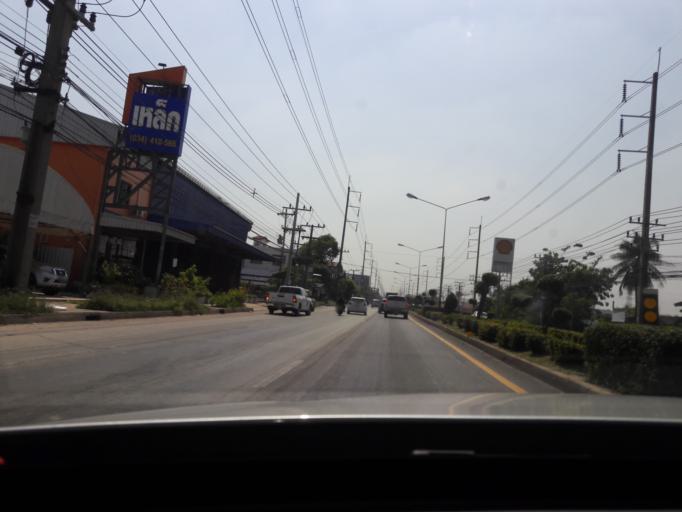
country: TH
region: Samut Sakhon
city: Krathum Baen
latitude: 13.6117
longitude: 100.2882
